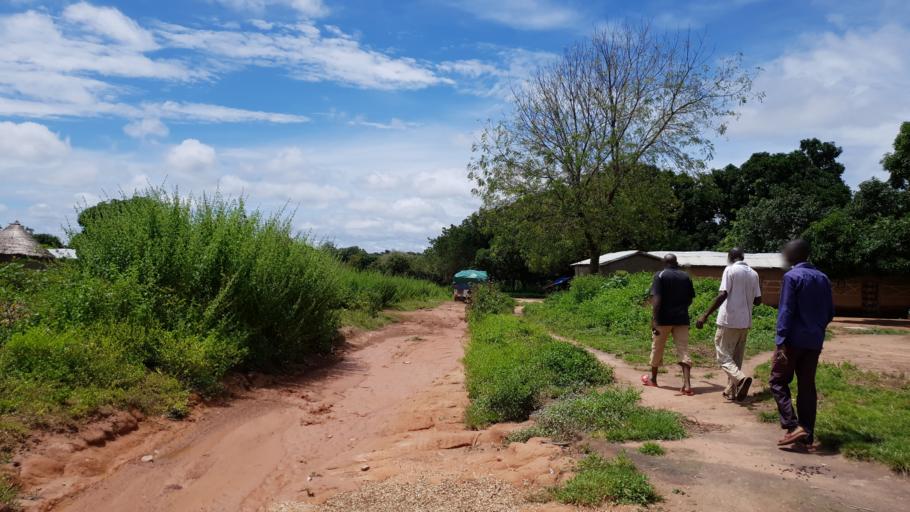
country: CI
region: Savanes
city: Tengrela
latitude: 10.3577
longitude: -6.9185
